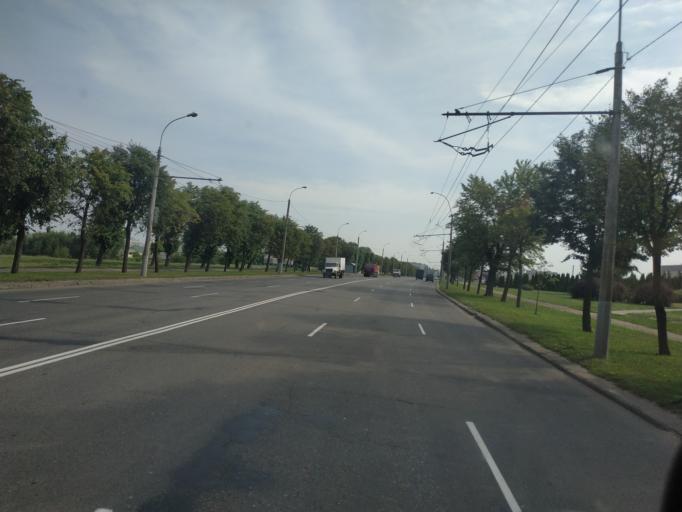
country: BY
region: Mogilev
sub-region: Mahilyowski Rayon
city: Veyno
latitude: 53.8654
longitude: 30.3602
